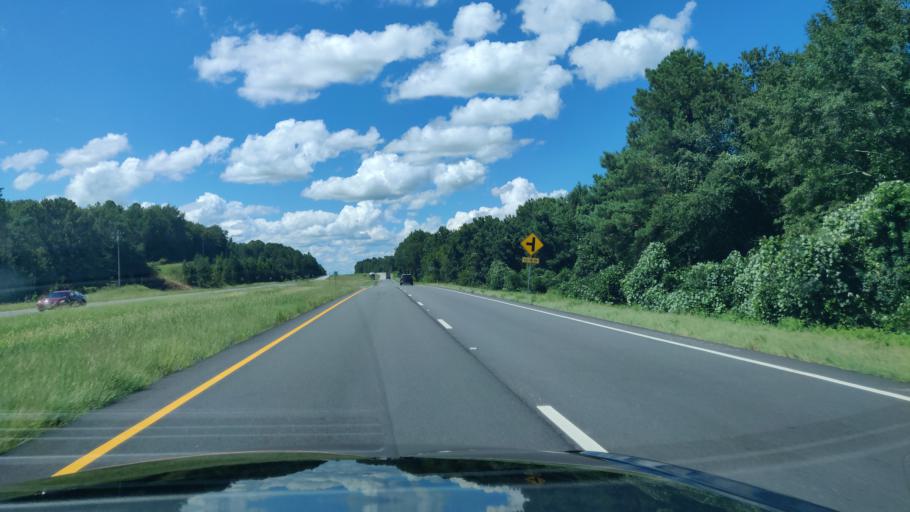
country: US
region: Georgia
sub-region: Chattahoochee County
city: Cusseta
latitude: 32.2281
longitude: -84.7118
